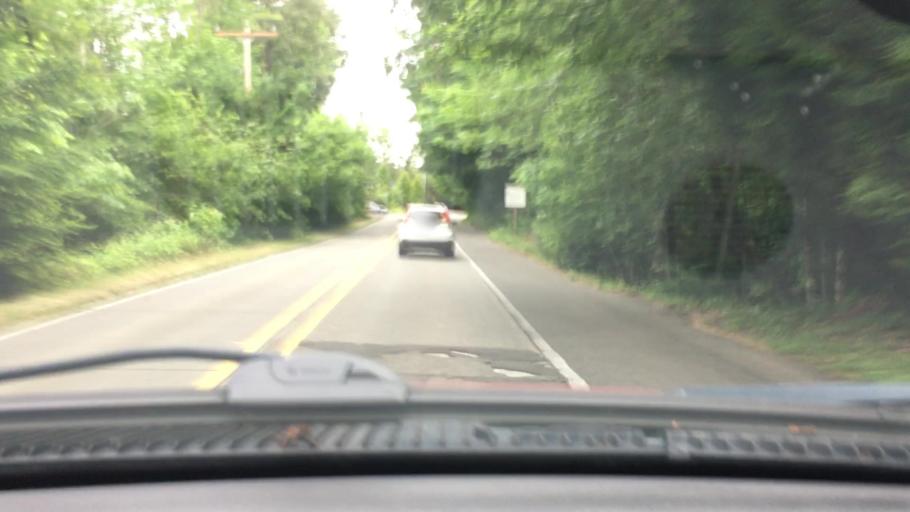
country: US
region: Washington
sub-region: King County
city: Sammamish
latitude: 47.6175
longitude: -122.0995
